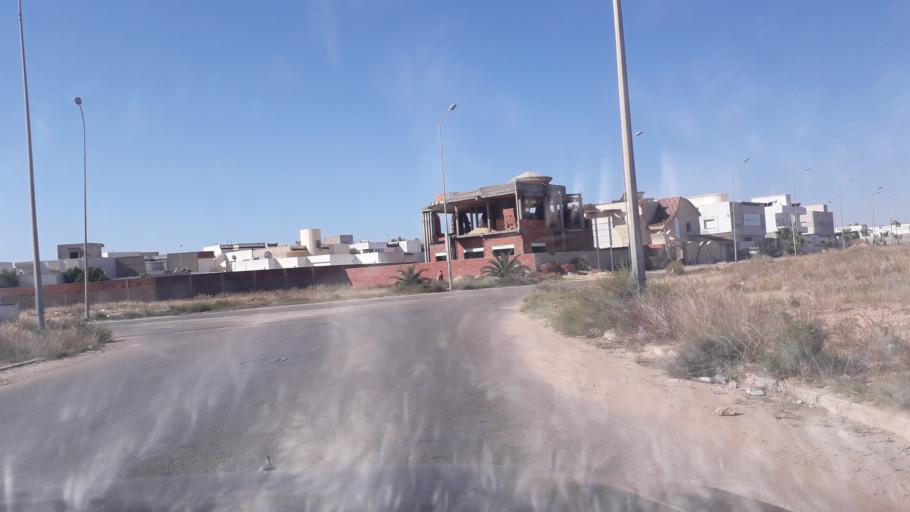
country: TN
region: Safaqis
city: Al Qarmadah
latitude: 34.8285
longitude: 10.7534
